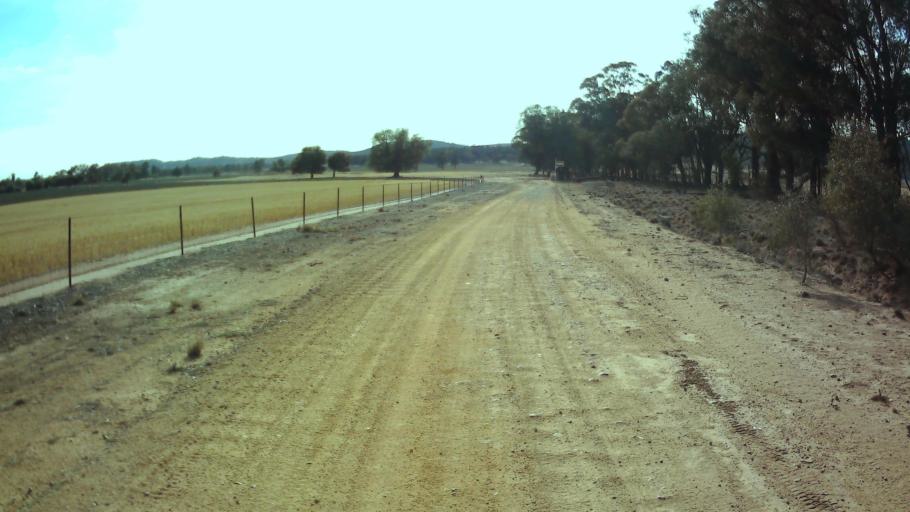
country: AU
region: New South Wales
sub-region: Weddin
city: Grenfell
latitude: -33.7968
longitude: 148.0947
